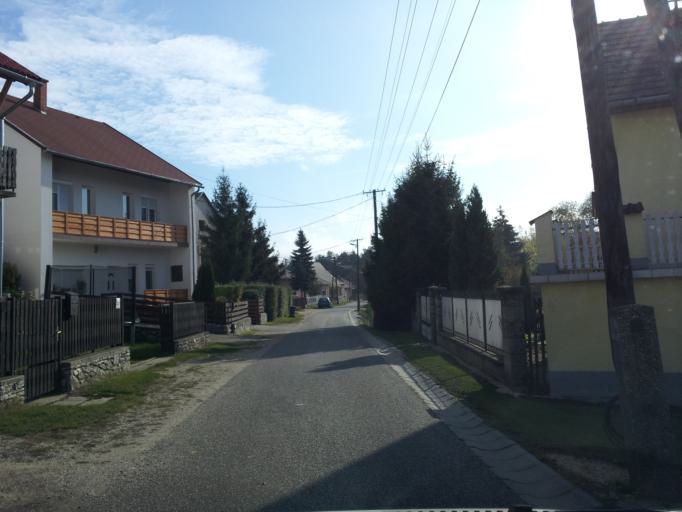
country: HU
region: Gyor-Moson-Sopron
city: Bakonyszentlaszlo
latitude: 47.3817
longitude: 17.8055
